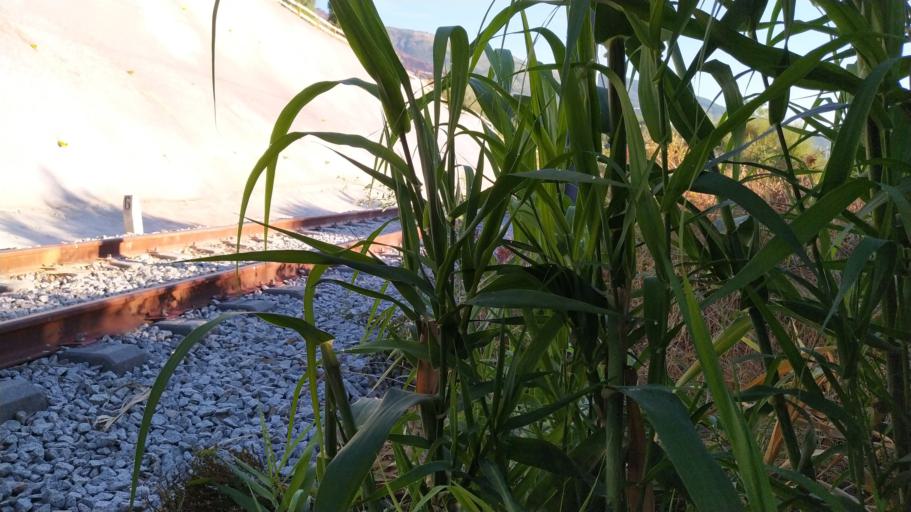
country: PT
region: Castelo Branco
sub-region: Covilha
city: Covilha
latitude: 40.2813
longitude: -7.4961
